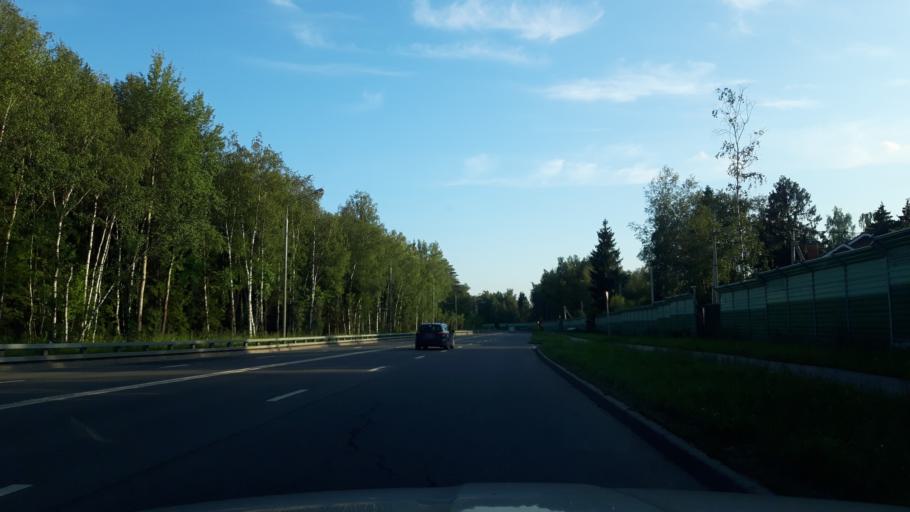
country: RU
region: Moskovskaya
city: Alabushevo
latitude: 56.0049
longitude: 37.1658
